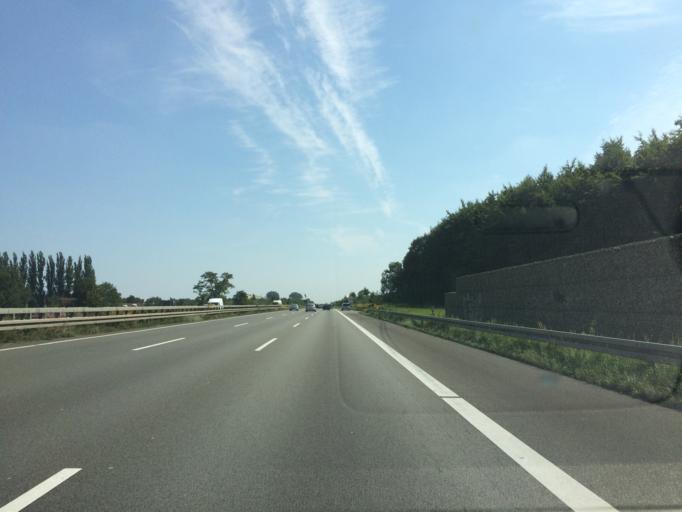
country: DE
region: North Rhine-Westphalia
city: Waltrop
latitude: 51.5821
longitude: 7.4336
